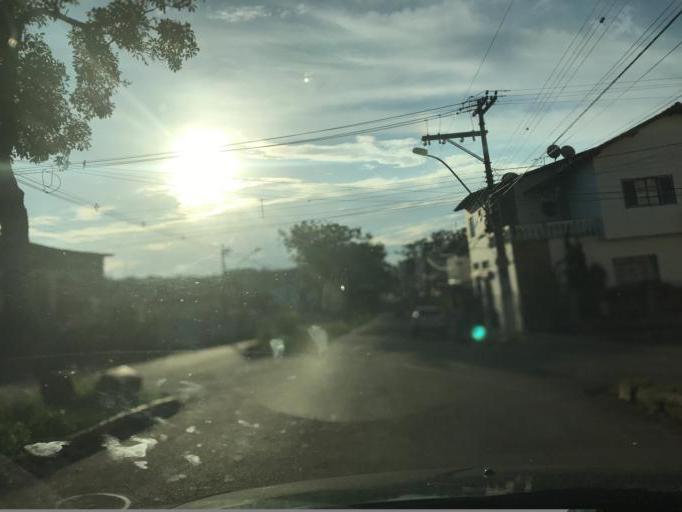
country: BR
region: Minas Gerais
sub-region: Tres Coracoes
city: Tres Coracoes
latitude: -21.7034
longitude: -45.2510
